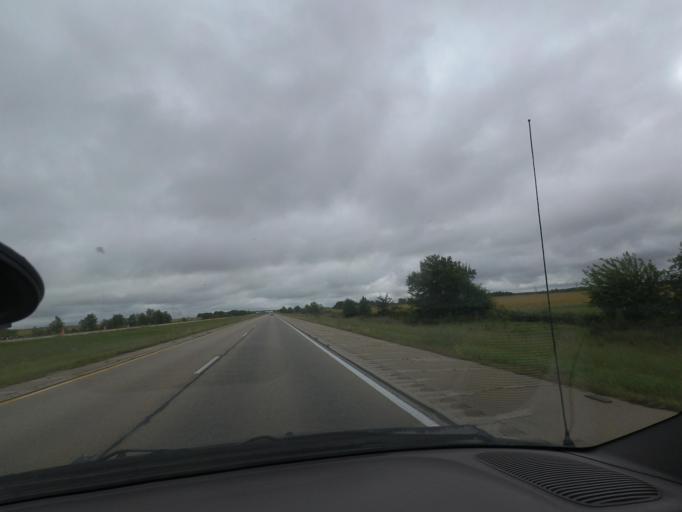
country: US
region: Illinois
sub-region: Piatt County
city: Monticello
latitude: 40.0221
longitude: -88.6983
